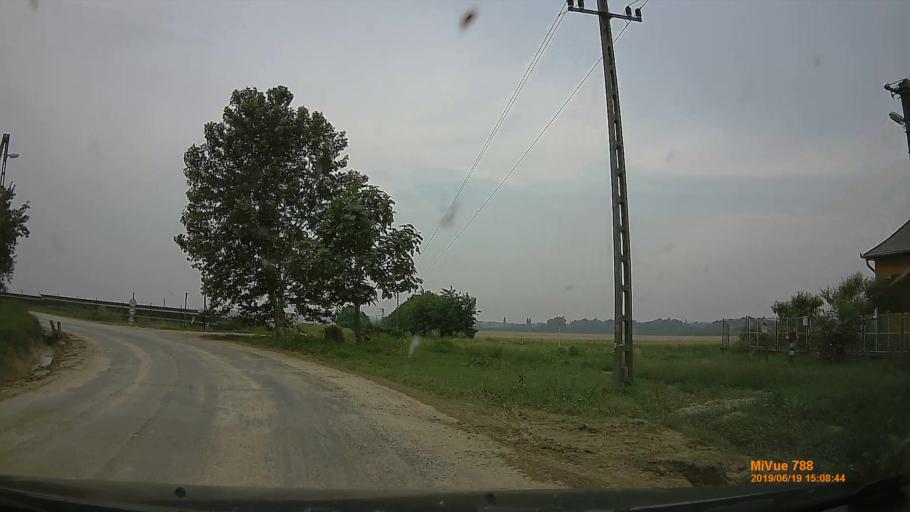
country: HU
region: Baranya
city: Szigetvar
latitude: 46.0877
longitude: 17.7977
